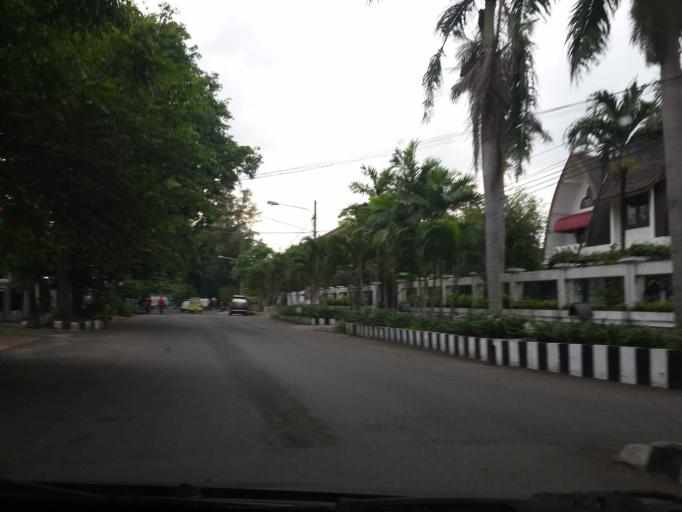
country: ID
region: East Java
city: Gubengairlangga
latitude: -7.2800
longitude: 112.7351
